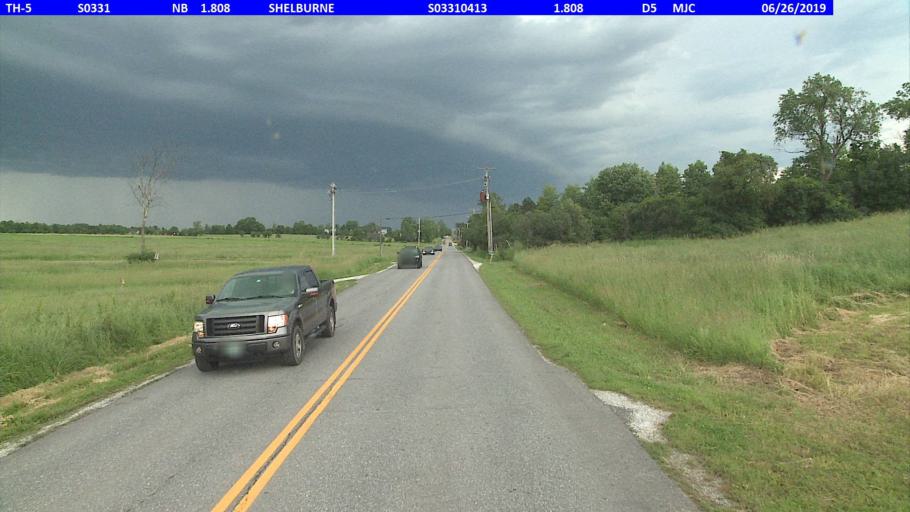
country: US
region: Vermont
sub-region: Chittenden County
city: South Burlington
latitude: 44.3966
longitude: -73.1764
